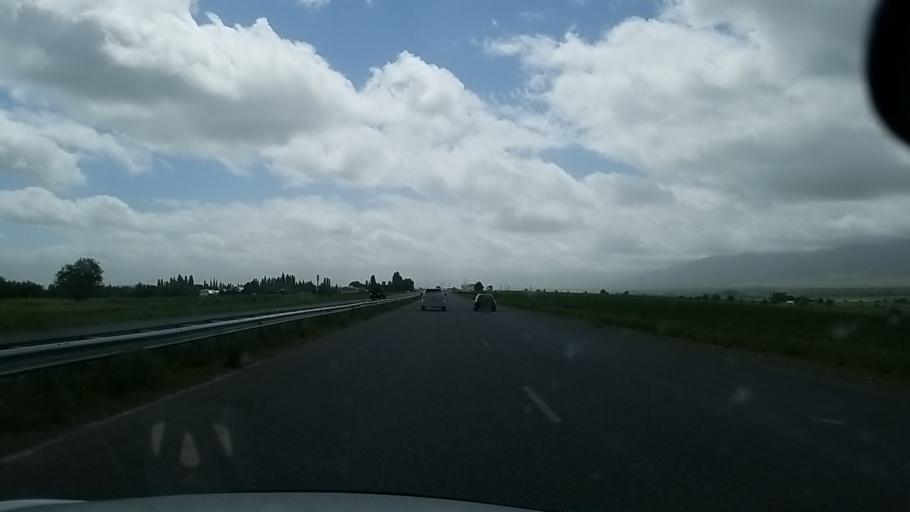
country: KZ
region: Ongtustik Qazaqstan
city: Kokterek
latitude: 42.5334
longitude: 70.2962
